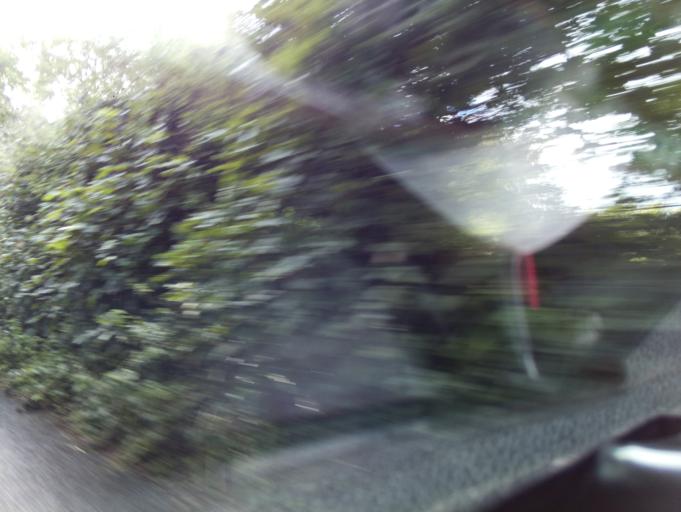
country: GB
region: England
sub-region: Devon
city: South Brent
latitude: 50.3980
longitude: -3.7943
